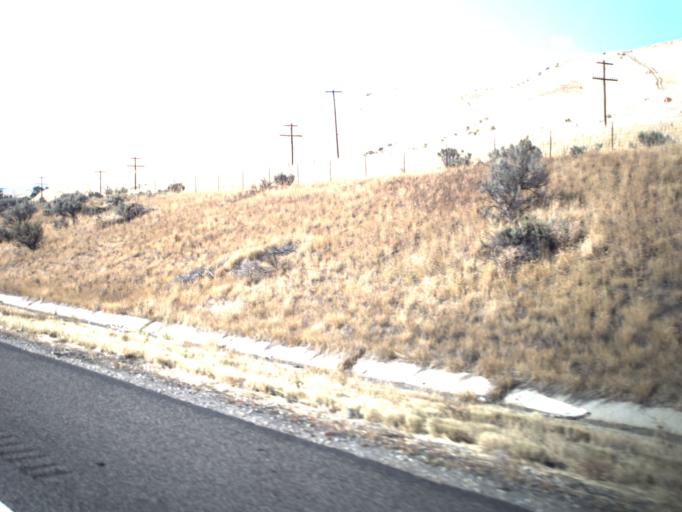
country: US
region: Utah
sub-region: Summit County
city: Coalville
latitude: 41.0065
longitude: -111.4763
